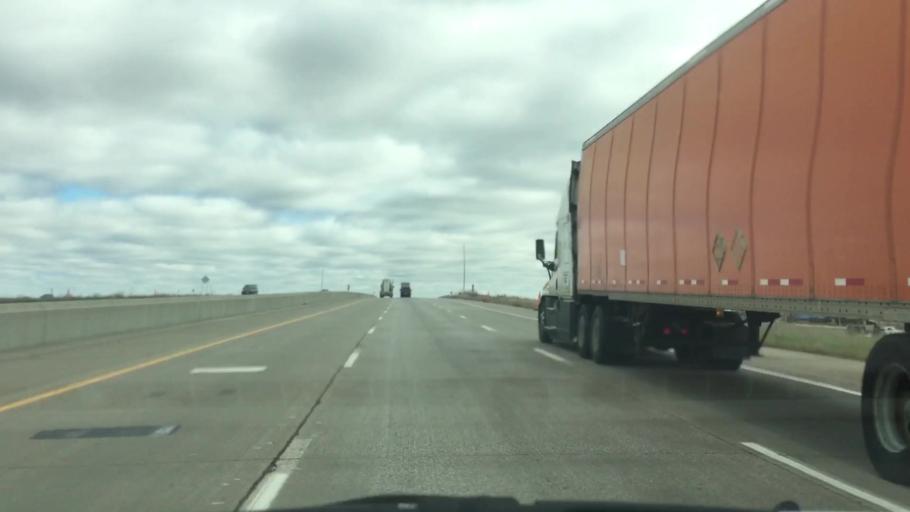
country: US
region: Iowa
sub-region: Polk County
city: Altoona
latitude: 41.6619
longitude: -93.4984
